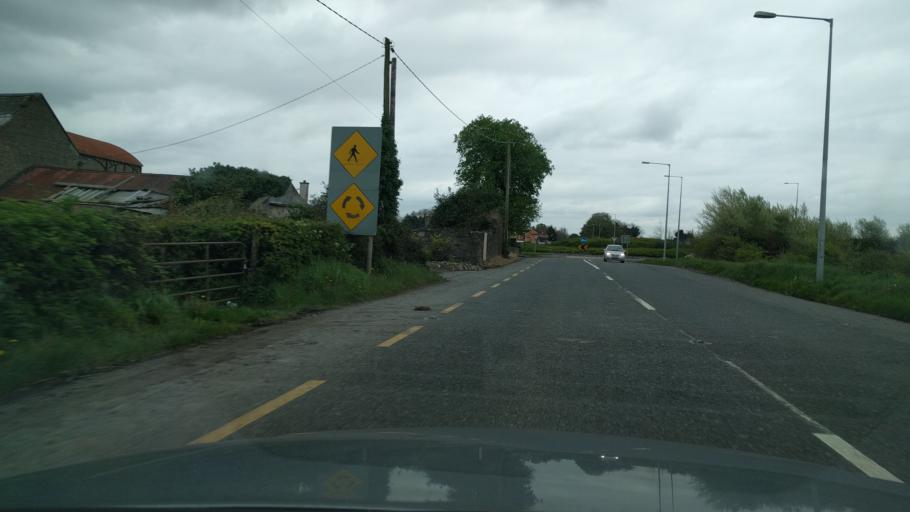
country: IE
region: Leinster
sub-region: Dublin City
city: Finglas
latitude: 53.4360
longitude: -6.3347
